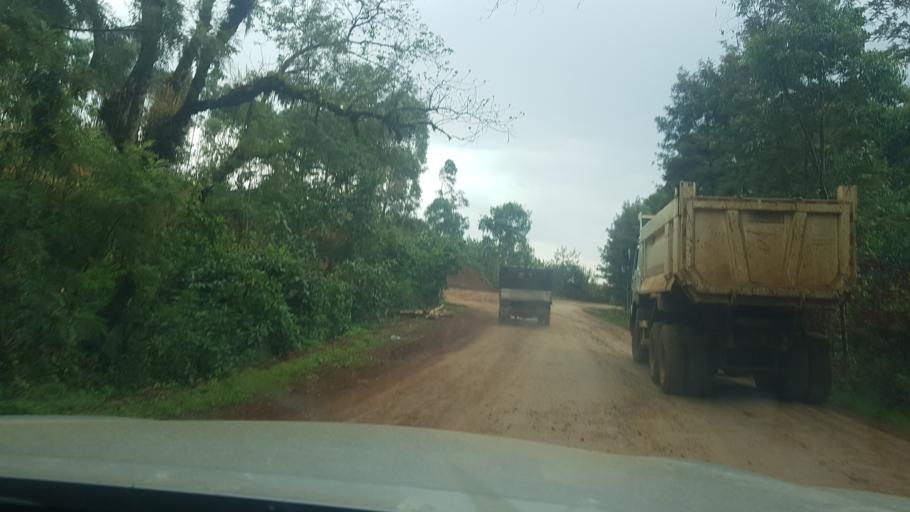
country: ET
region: Oromiya
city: Gore
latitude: 7.8951
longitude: 35.4918
